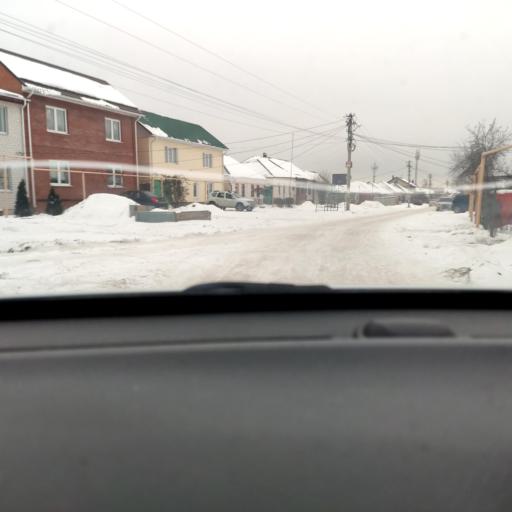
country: RU
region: Voronezj
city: Somovo
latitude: 51.7504
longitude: 39.3415
